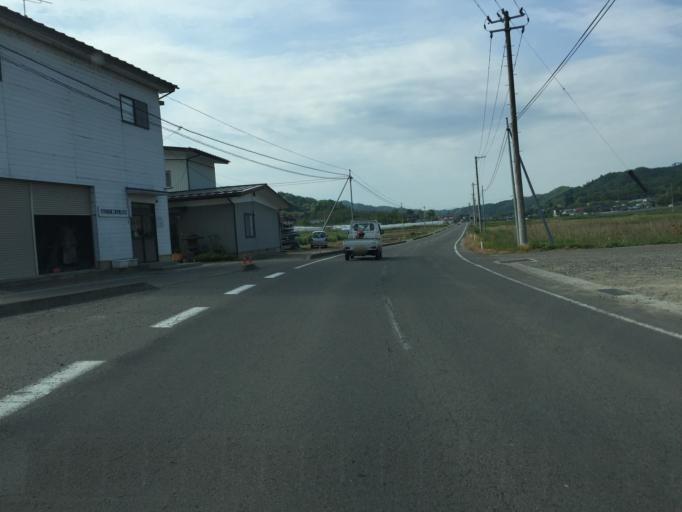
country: JP
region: Fukushima
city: Yanagawamachi-saiwaicho
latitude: 37.7988
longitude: 140.6232
